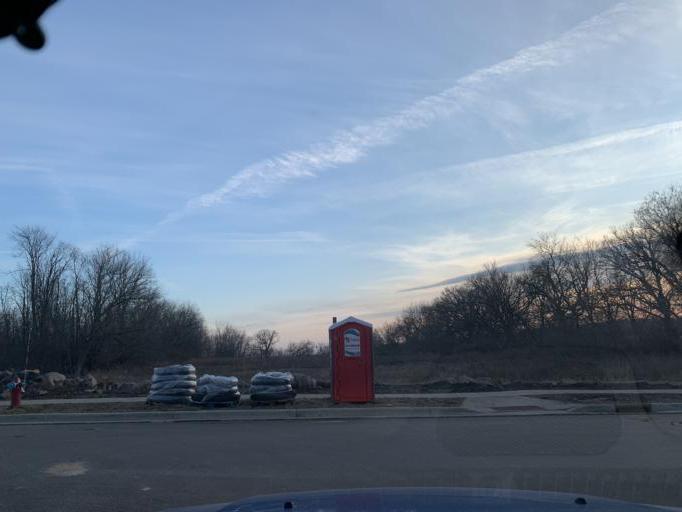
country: US
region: Wisconsin
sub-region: Dane County
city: Verona
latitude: 43.0552
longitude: -89.5662
